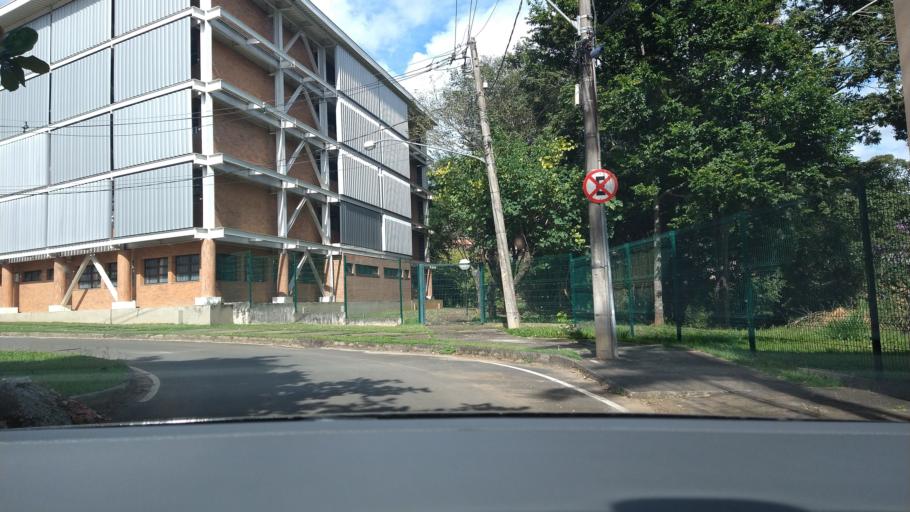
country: BR
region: Minas Gerais
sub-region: Vicosa
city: Vicosa
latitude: -20.7634
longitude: -42.8695
